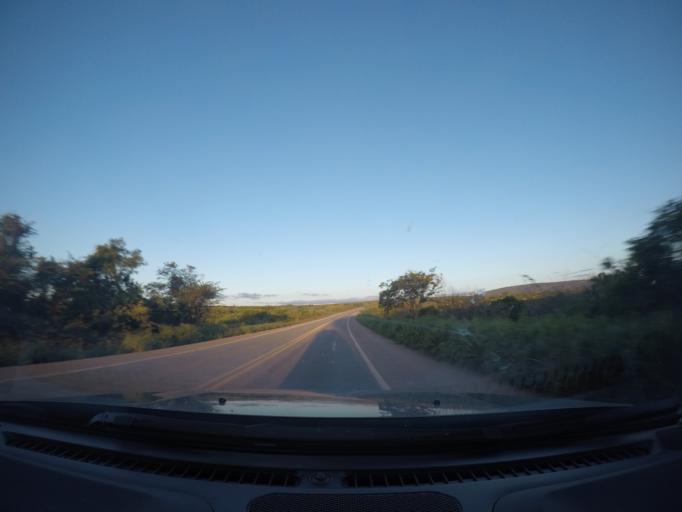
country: BR
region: Bahia
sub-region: Seabra
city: Seabra
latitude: -12.3940
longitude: -41.9273
